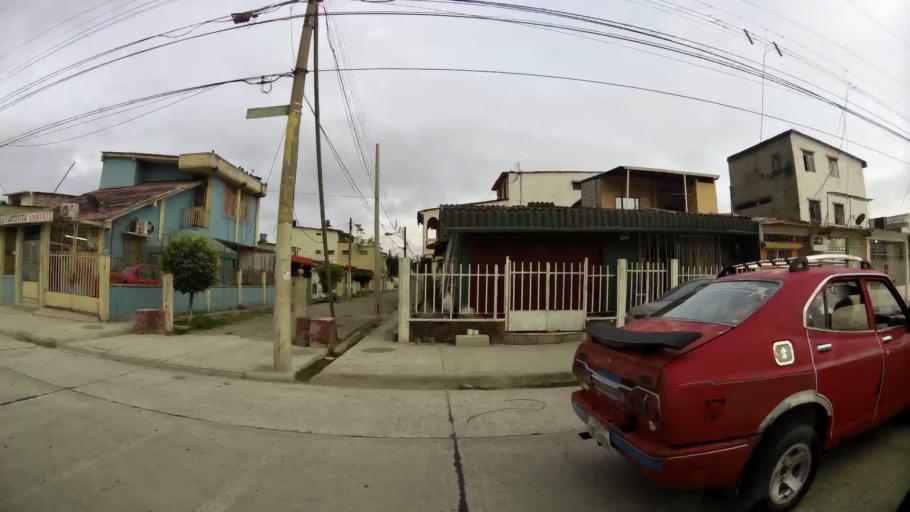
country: EC
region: Guayas
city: Eloy Alfaro
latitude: -2.1733
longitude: -79.8841
